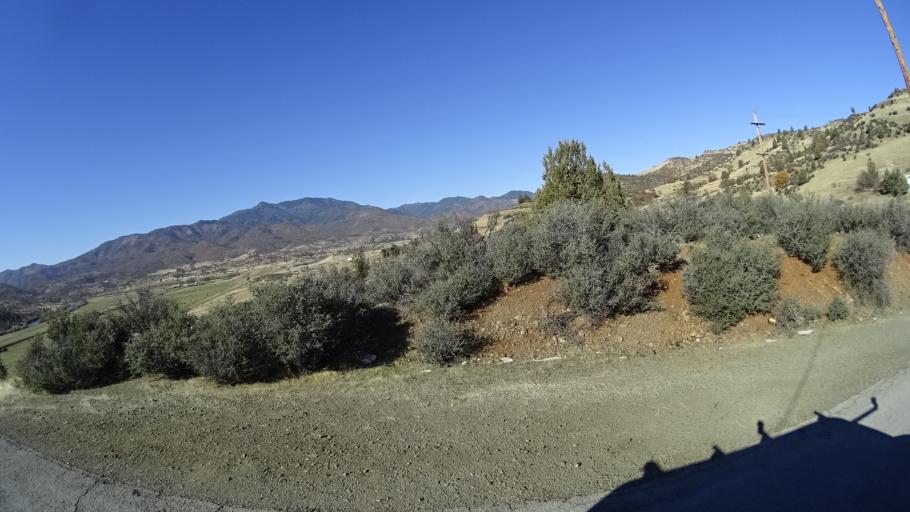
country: US
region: California
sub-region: Siskiyou County
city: Montague
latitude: 41.8983
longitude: -122.5237
